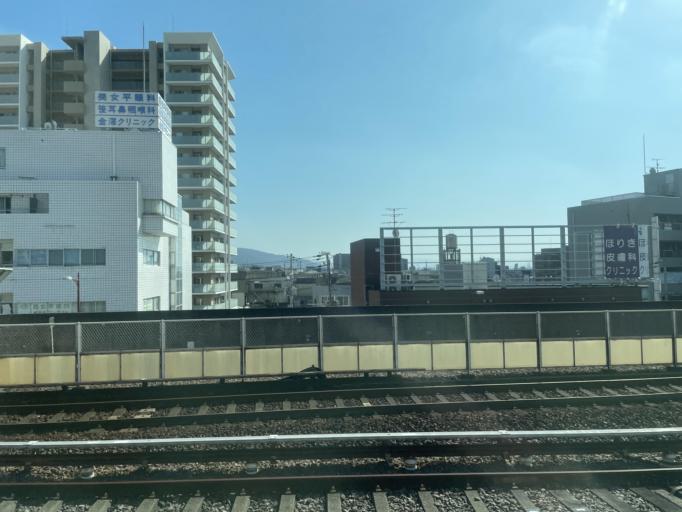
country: JP
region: Osaka
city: Daitocho
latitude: 34.6802
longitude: 135.6424
